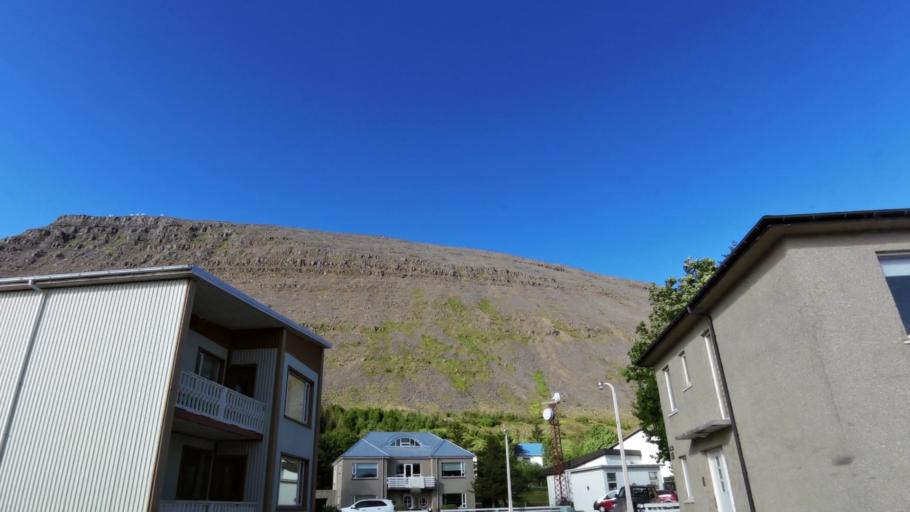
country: IS
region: West
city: Olafsvik
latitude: 65.5977
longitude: -23.9987
